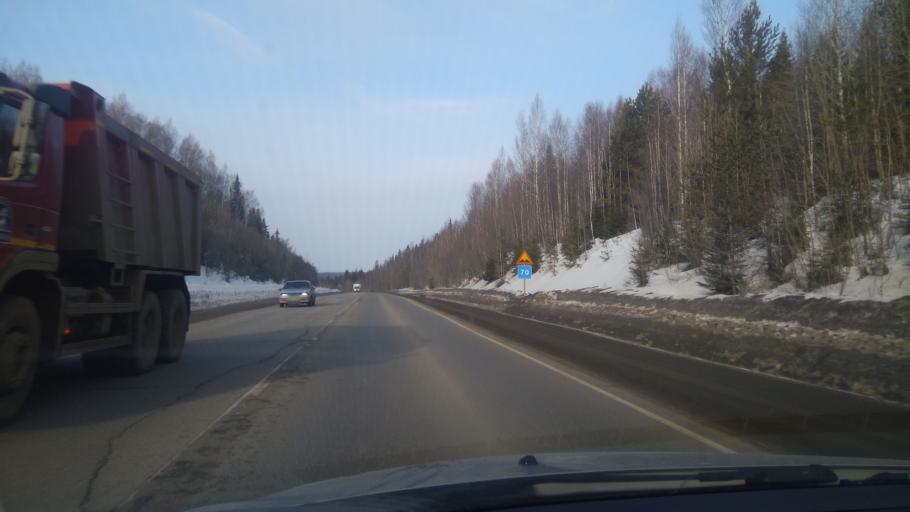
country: RU
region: Sverdlovsk
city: Bisert'
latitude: 56.8272
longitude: 59.2102
